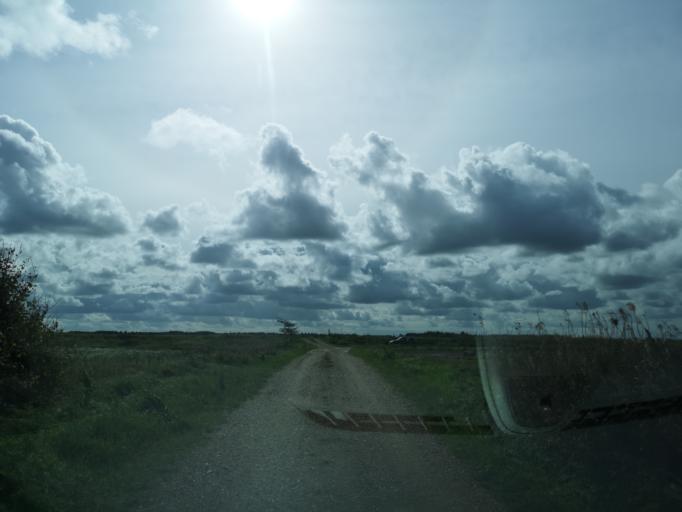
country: DK
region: Central Jutland
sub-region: Ringkobing-Skjern Kommune
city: Tarm
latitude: 55.9315
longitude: 8.5372
